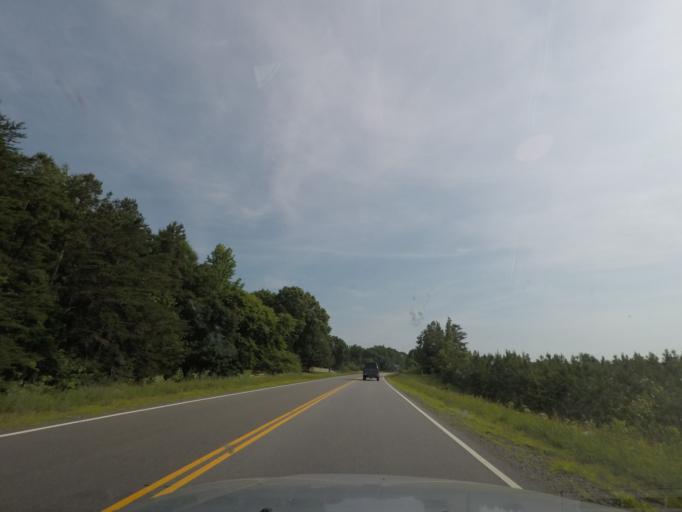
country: US
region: Virginia
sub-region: Mecklenburg County
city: Chase City
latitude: 36.8088
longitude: -78.6007
